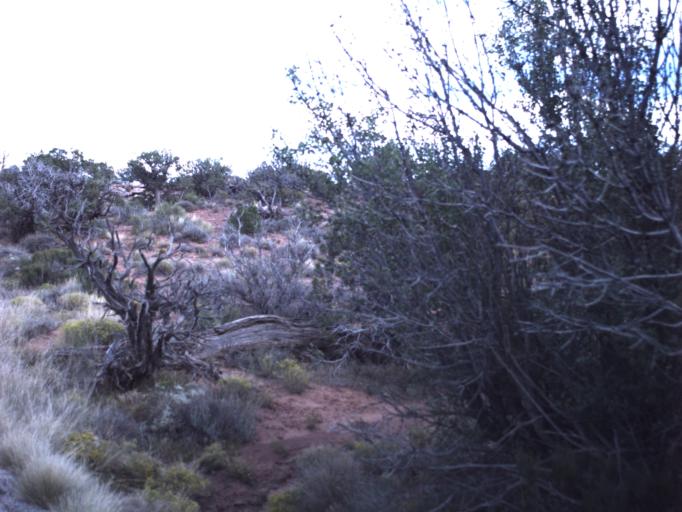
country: US
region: Utah
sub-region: Grand County
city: Moab
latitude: 38.4768
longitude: -109.7417
